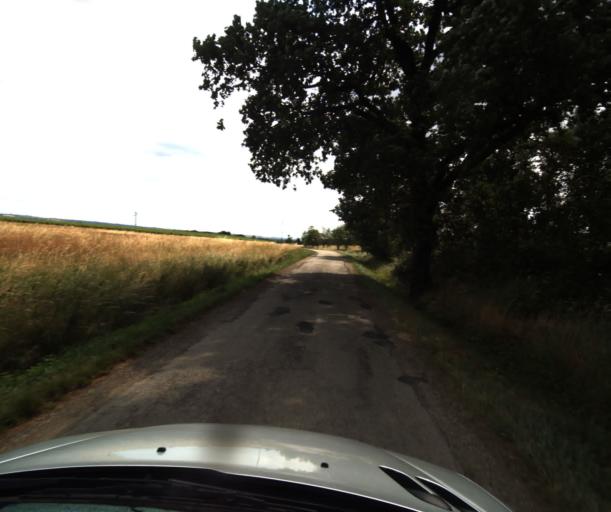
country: FR
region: Midi-Pyrenees
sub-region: Departement du Tarn-et-Garonne
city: Campsas
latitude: 43.9097
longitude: 1.3027
